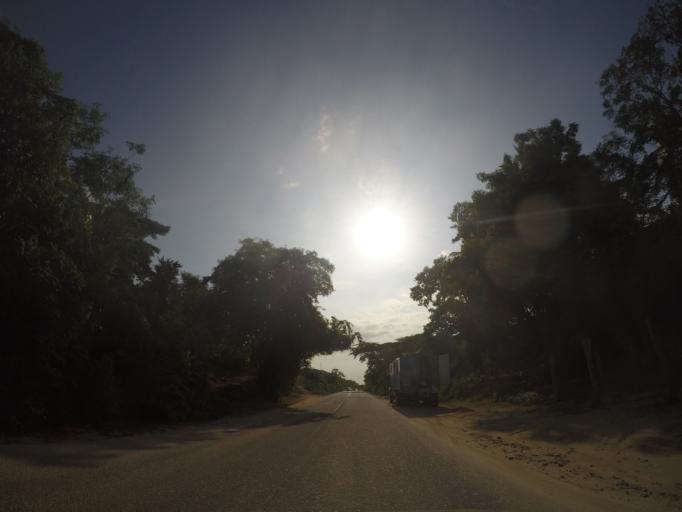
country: MX
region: Oaxaca
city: San Pedro Pochutla
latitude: 15.7320
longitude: -96.5045
